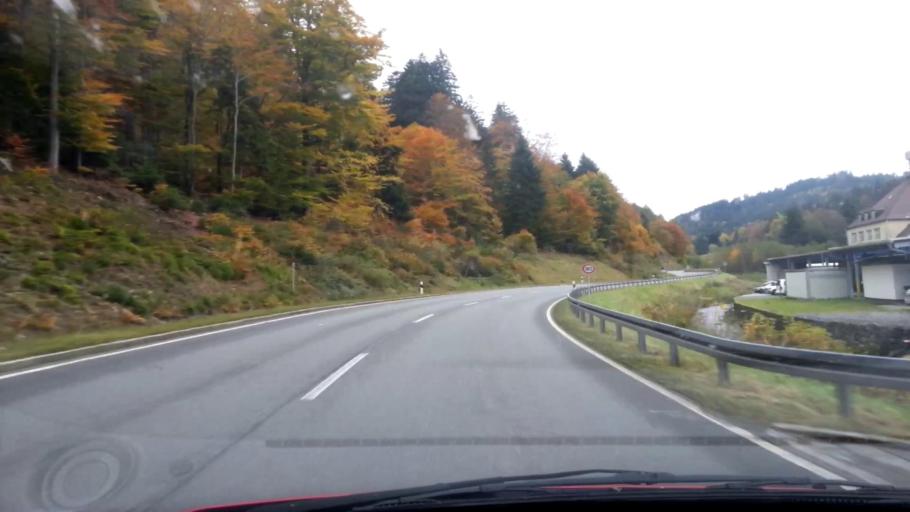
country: DE
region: Bavaria
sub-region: Upper Franconia
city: Warmensteinach
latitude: 49.9664
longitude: 11.7647
